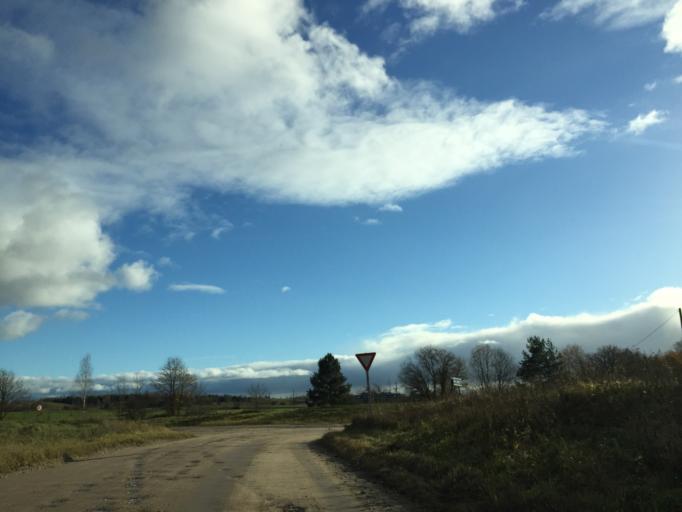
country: LV
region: Tukuma Rajons
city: Tukums
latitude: 56.9683
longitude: 22.9622
